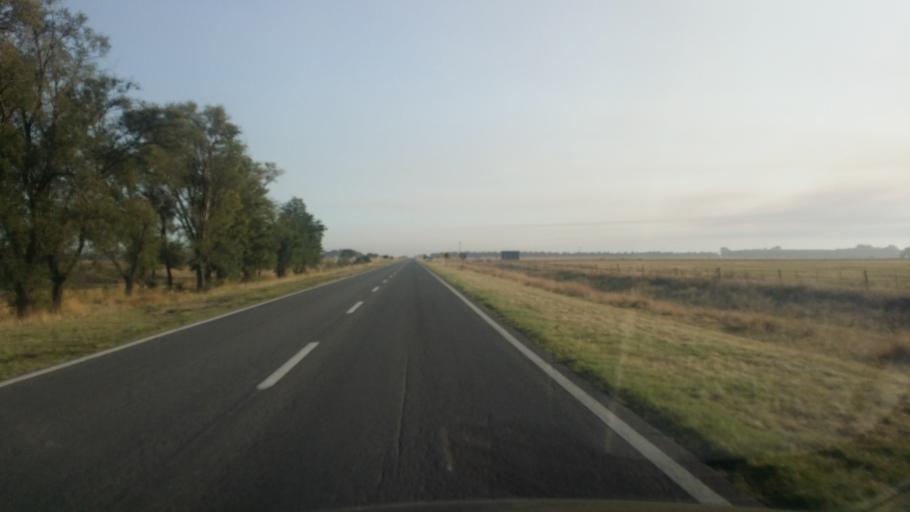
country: AR
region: La Pampa
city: Santa Rosa
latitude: -36.4842
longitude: -64.2807
